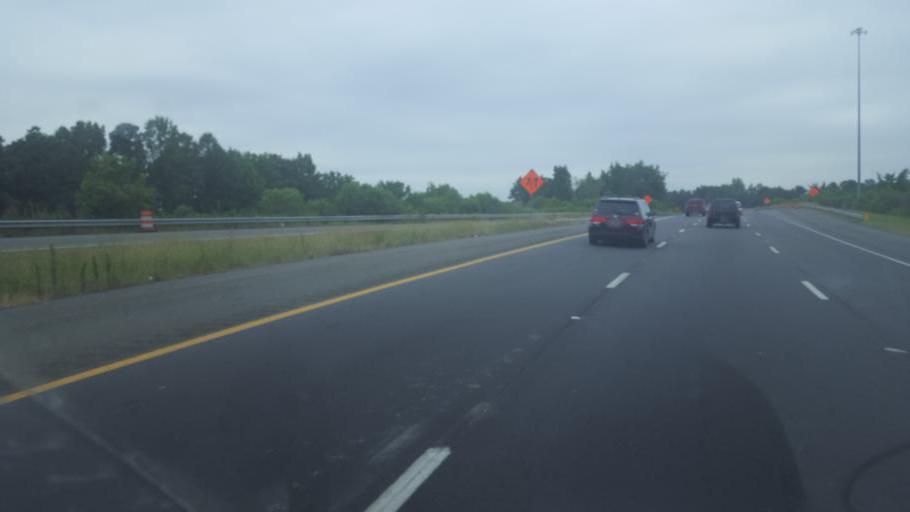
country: US
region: North Carolina
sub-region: Mecklenburg County
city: Charlotte
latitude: 35.2738
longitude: -80.8464
